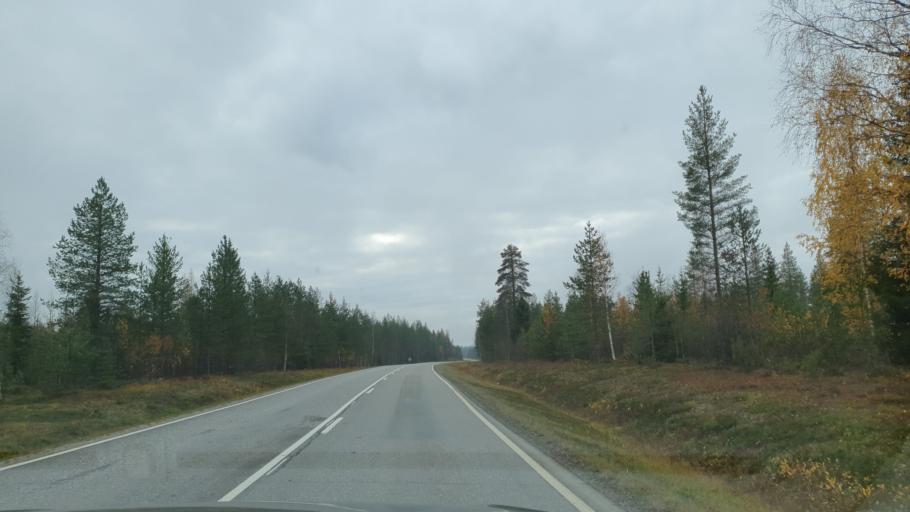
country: FI
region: Lapland
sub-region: Rovaniemi
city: Ranua
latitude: 66.0350
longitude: 26.3345
